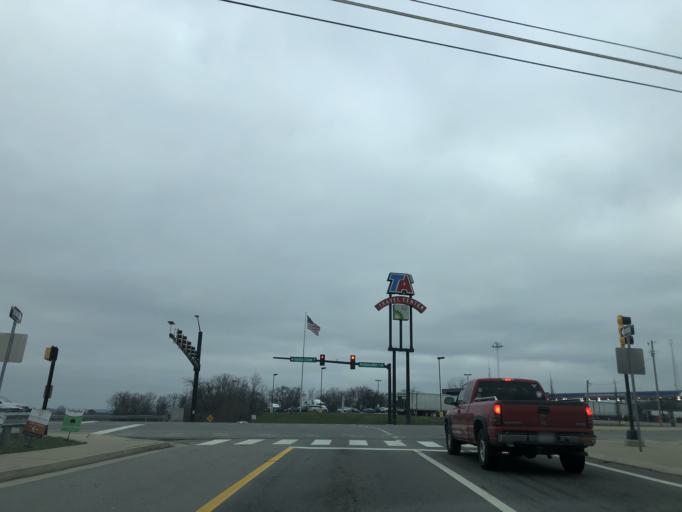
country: US
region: Tennessee
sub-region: Williamson County
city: Franklin
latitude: 35.8588
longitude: -86.8311
